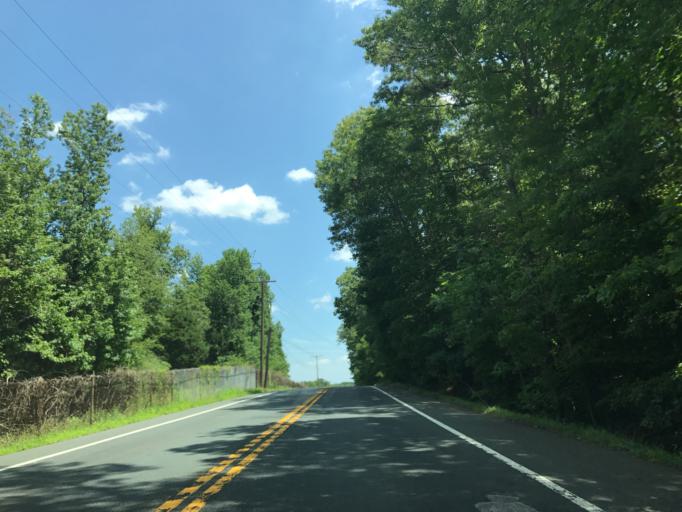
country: US
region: Maryland
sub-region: Anne Arundel County
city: Maryland City
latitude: 39.0467
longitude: -76.8048
